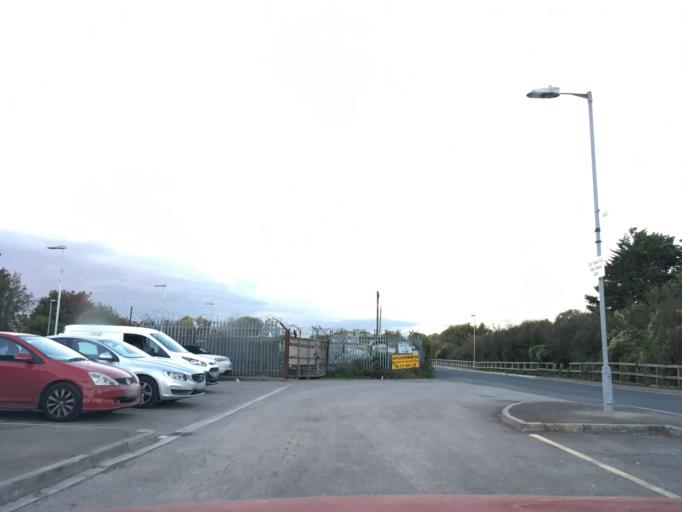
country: GB
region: England
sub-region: South Gloucestershire
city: Stoke Gifford
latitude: 51.5257
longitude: -2.5620
